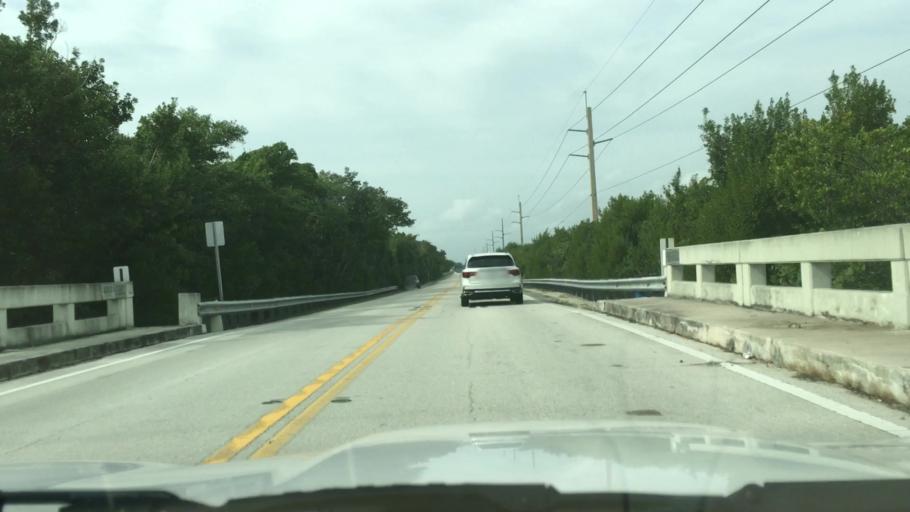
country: US
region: Florida
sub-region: Monroe County
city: North Key Largo
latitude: 25.2827
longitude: -80.3543
